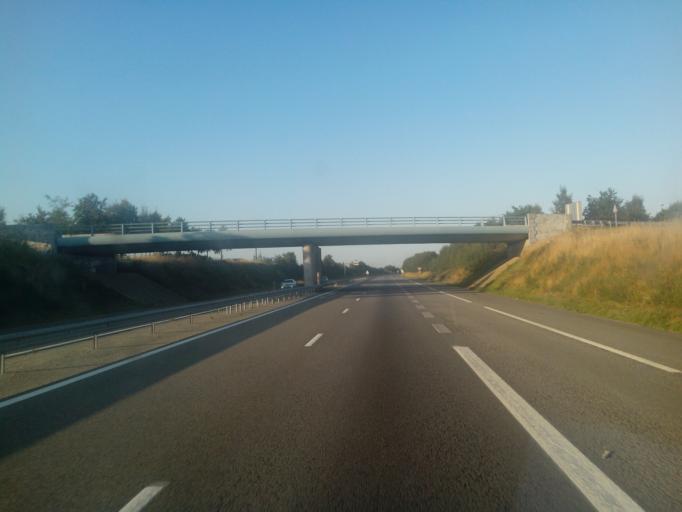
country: FR
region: Brittany
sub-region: Departement du Morbihan
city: Saint-Gonnery
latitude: 48.1221
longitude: -2.8506
